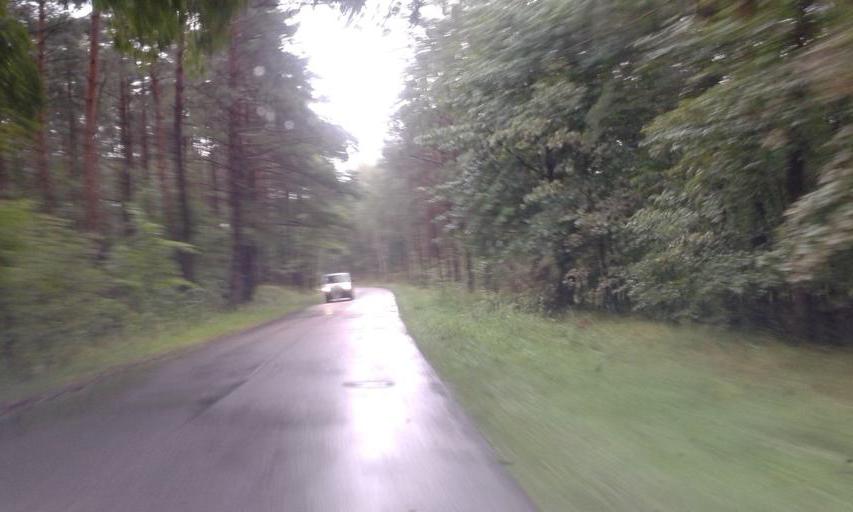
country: PL
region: West Pomeranian Voivodeship
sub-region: Powiat szczecinecki
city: Borne Sulinowo
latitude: 53.5148
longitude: 16.4936
